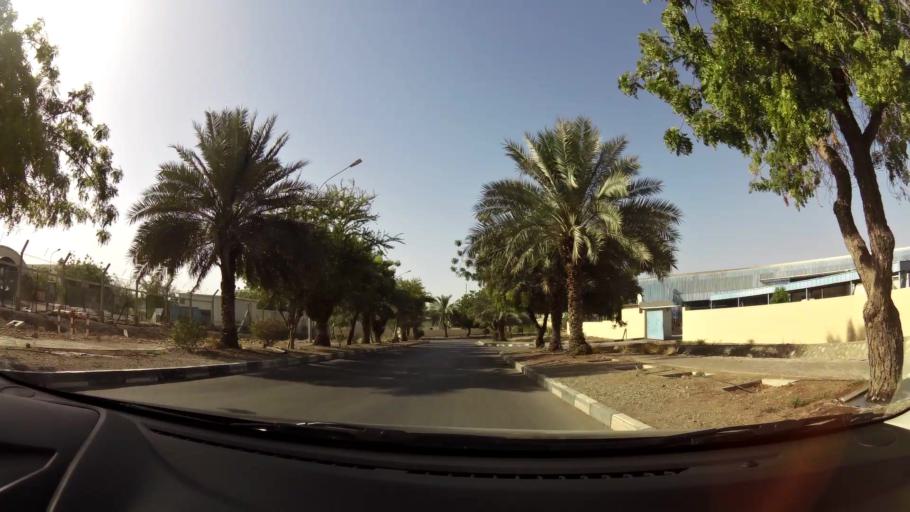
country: OM
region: Muhafazat Masqat
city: As Sib al Jadidah
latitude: 23.5544
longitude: 58.2018
